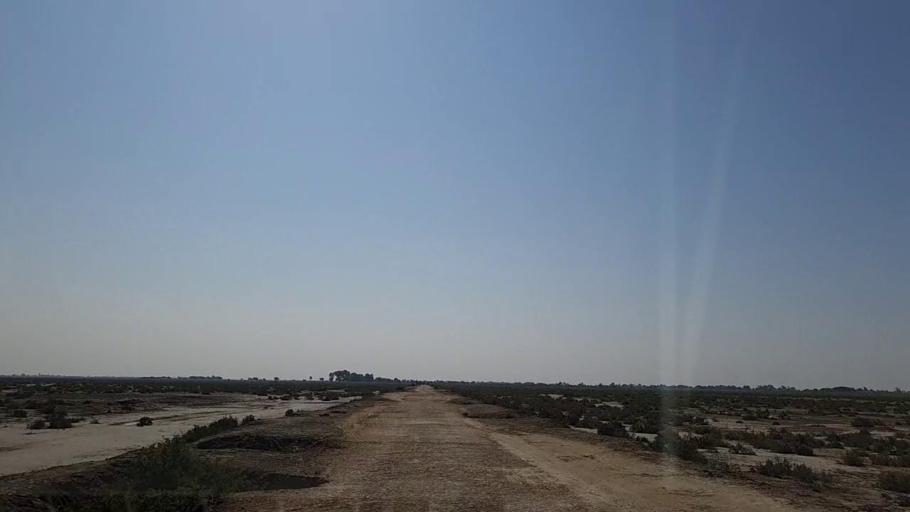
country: PK
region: Sindh
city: Chuhar Jamali
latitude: 24.5079
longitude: 68.0979
